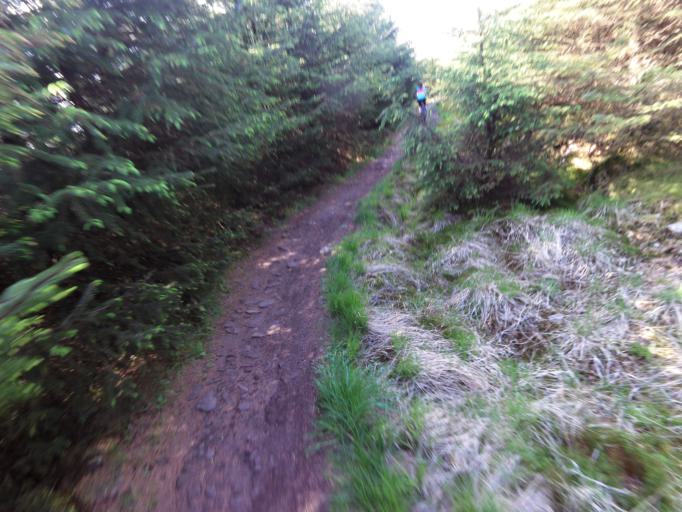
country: GB
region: England
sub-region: North Yorkshire
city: Settle
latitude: 54.0221
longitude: -2.3742
